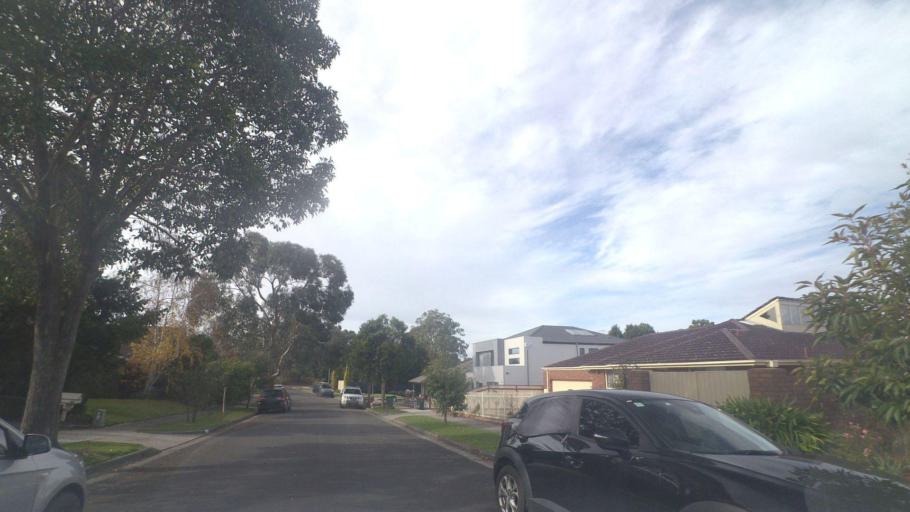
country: AU
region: Victoria
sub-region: Whitehorse
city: Vermont South
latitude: -37.8617
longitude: 145.1880
